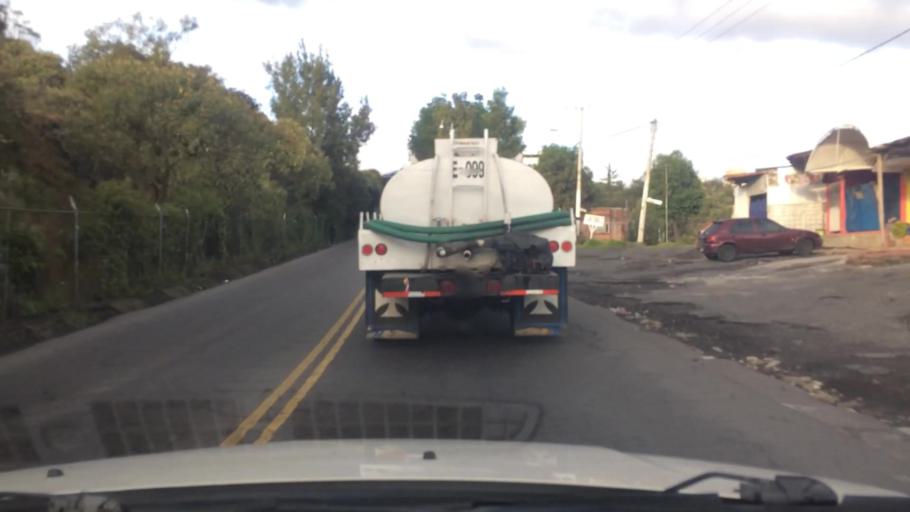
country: MX
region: Mexico City
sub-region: Tlalpan
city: Lomas de Tepemecatl
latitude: 19.2692
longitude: -99.2160
